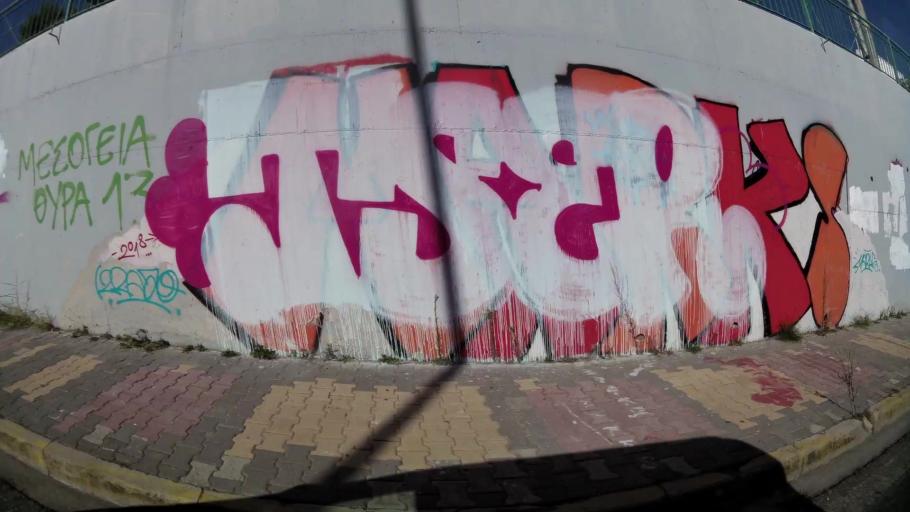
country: GR
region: Attica
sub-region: Nomarchia Anatolikis Attikis
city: Dhrafi
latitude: 38.0034
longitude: 23.8989
